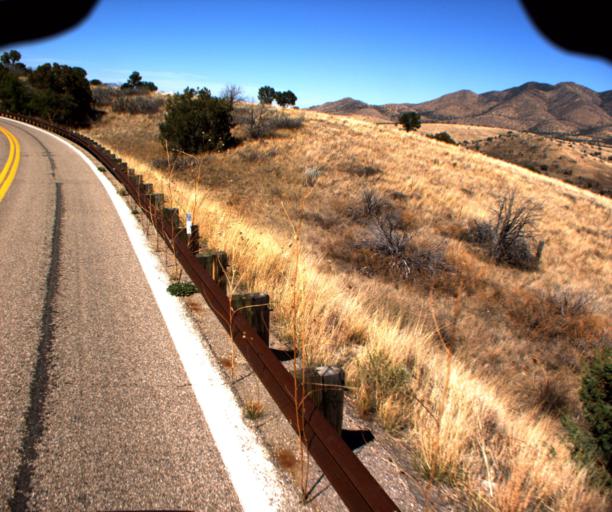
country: US
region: Arizona
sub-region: Cochise County
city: Sierra Vista
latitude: 31.5039
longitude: -110.4953
